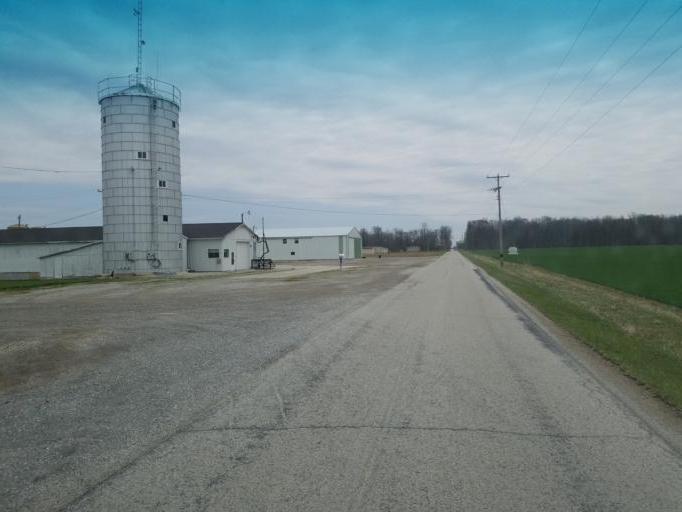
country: US
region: Ohio
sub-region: Crawford County
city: Bucyrus
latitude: 40.8921
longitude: -82.9761
